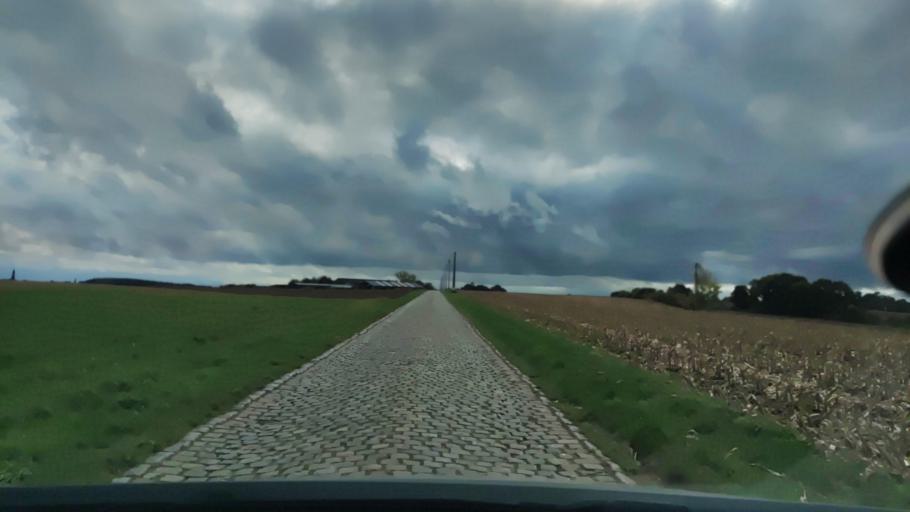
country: BE
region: Wallonia
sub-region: Province du Brabant Wallon
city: Jodoigne
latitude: 50.7344
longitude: 4.8616
